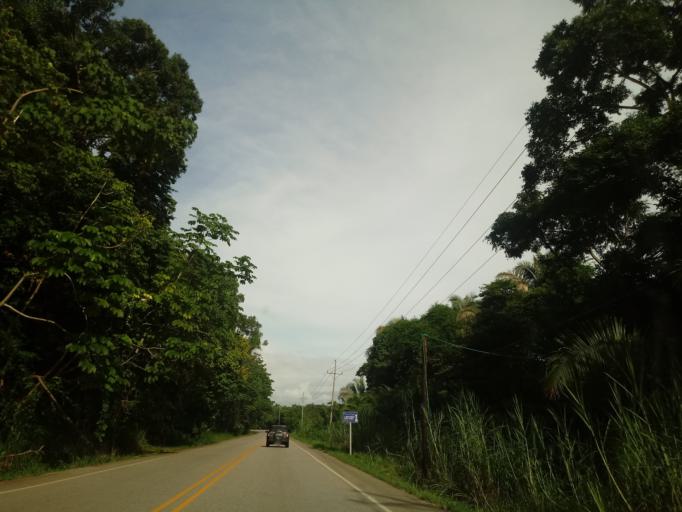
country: CR
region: San Jose
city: Daniel Flores
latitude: 9.1925
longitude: -83.7778
